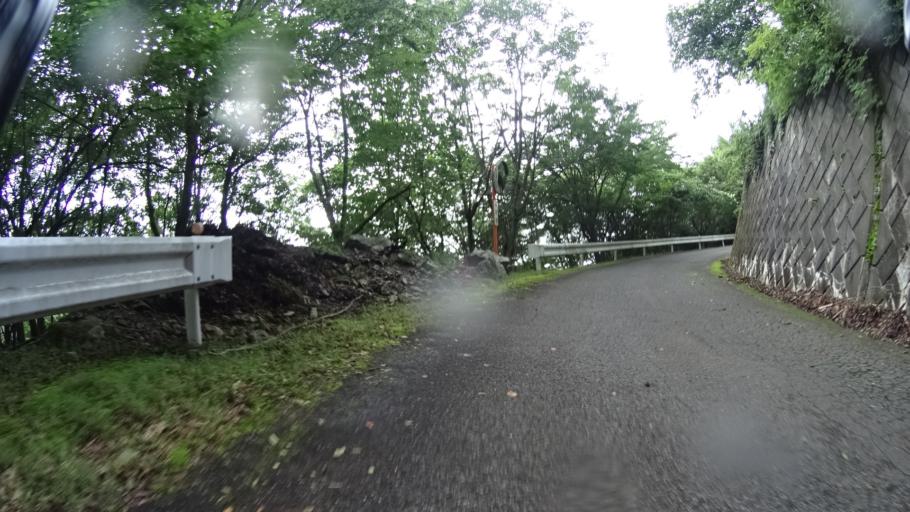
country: JP
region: Saitama
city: Chichibu
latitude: 35.8922
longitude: 139.1239
